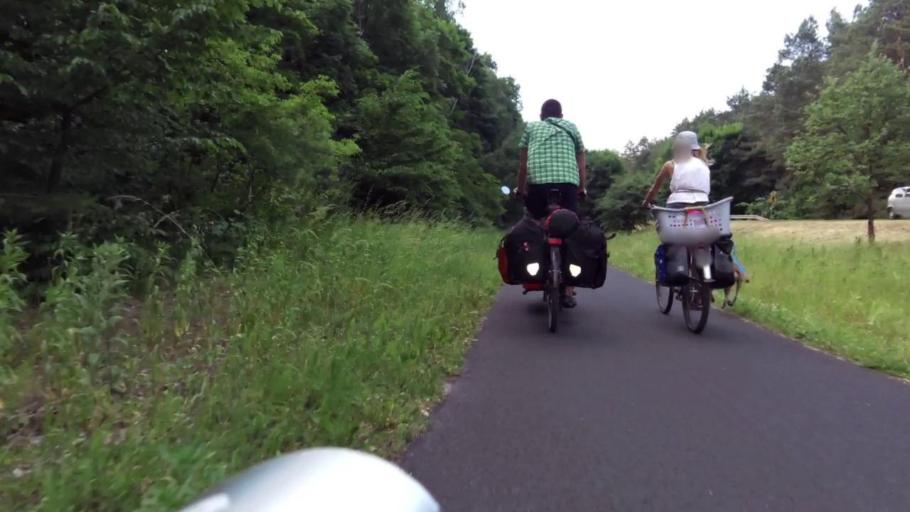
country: PL
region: Kujawsko-Pomorskie
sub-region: Powiat torunski
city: Lysomice
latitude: 53.0791
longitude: 18.5406
